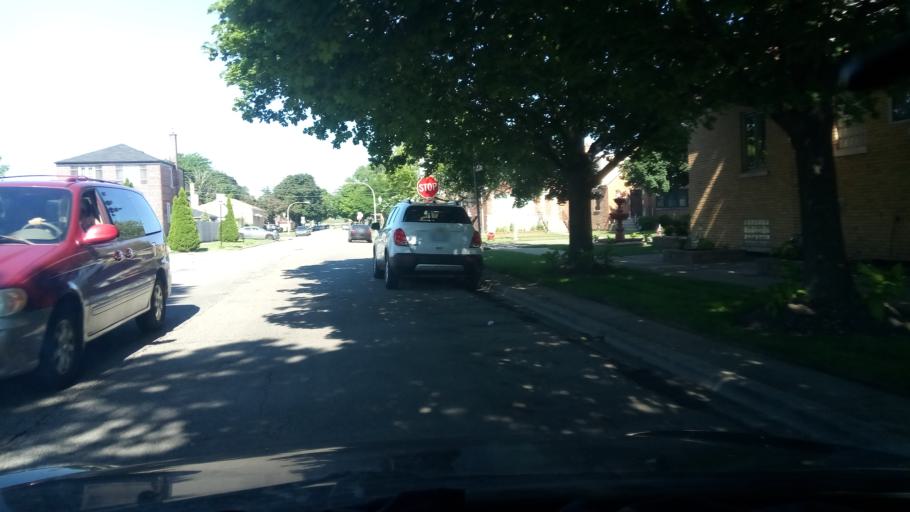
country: US
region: Illinois
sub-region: Cook County
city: Hometown
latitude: 41.7694
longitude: -87.7315
